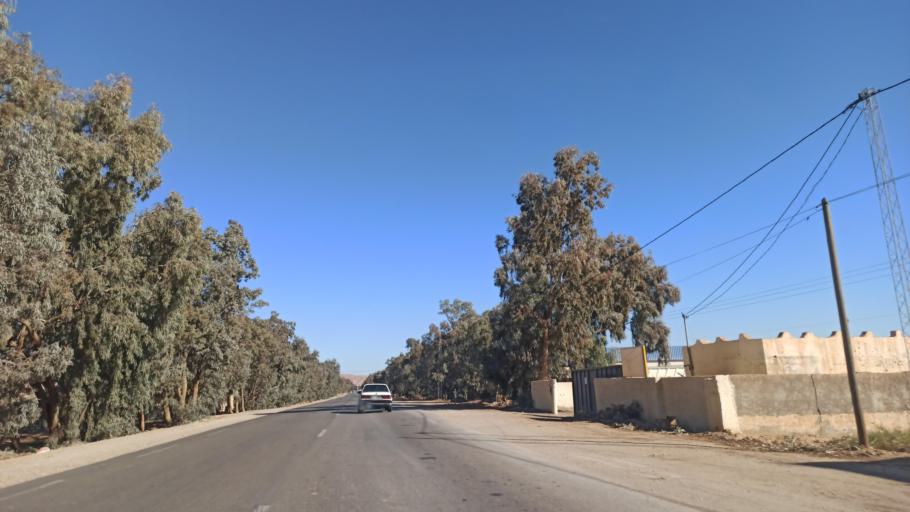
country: TN
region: Gafsa
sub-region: Gafsa Municipality
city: Gafsa
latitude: 34.3929
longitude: 8.7143
